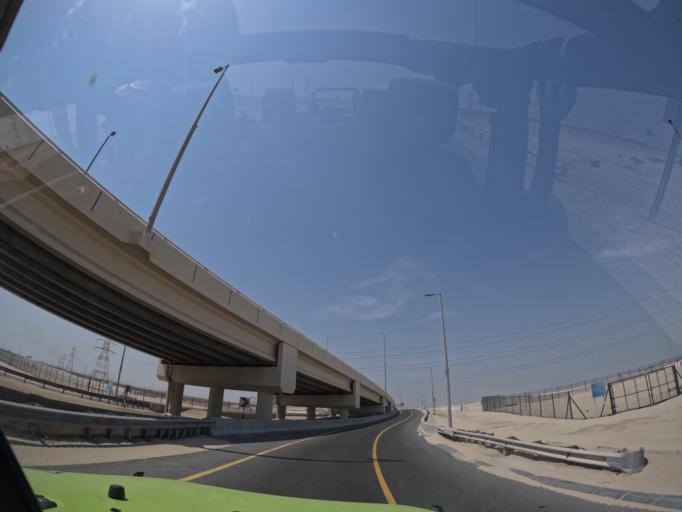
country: AE
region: Abu Dhabi
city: Abu Dhabi
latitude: 24.1644
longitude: 54.3541
